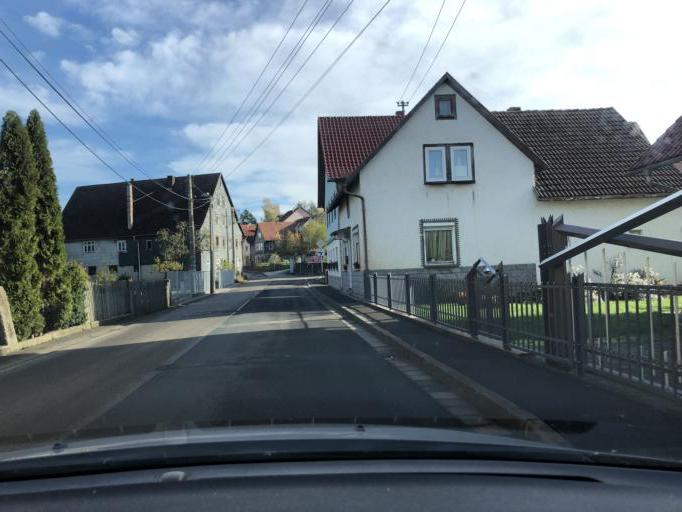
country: DE
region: Thuringia
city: Reurieth
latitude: 50.4531
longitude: 10.6517
